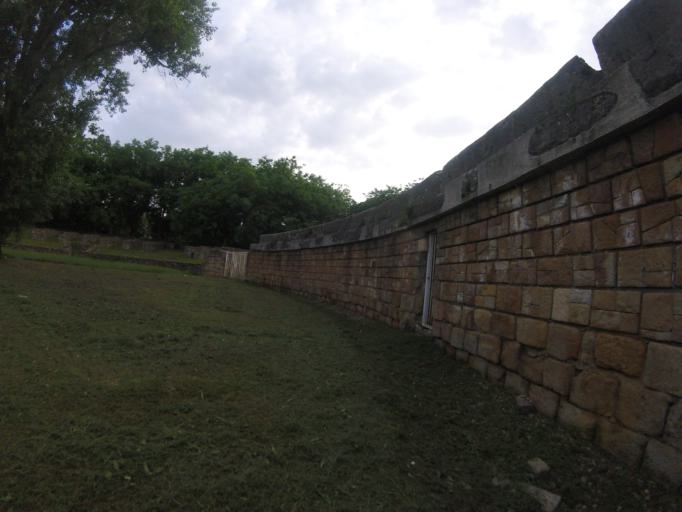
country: HU
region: Budapest
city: Budapest III. keruelet
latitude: 47.5677
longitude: 19.0478
